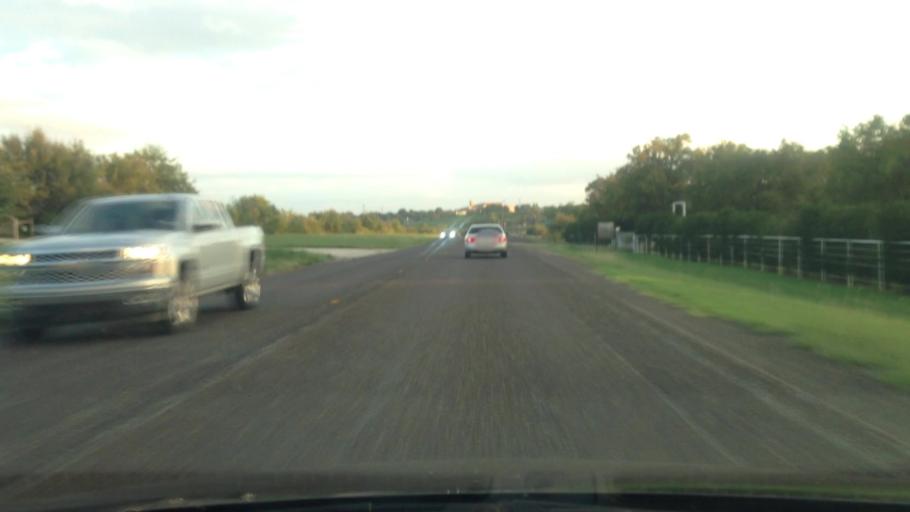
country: US
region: Texas
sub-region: Tarrant County
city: Benbrook
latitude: 32.6849
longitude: -97.4991
